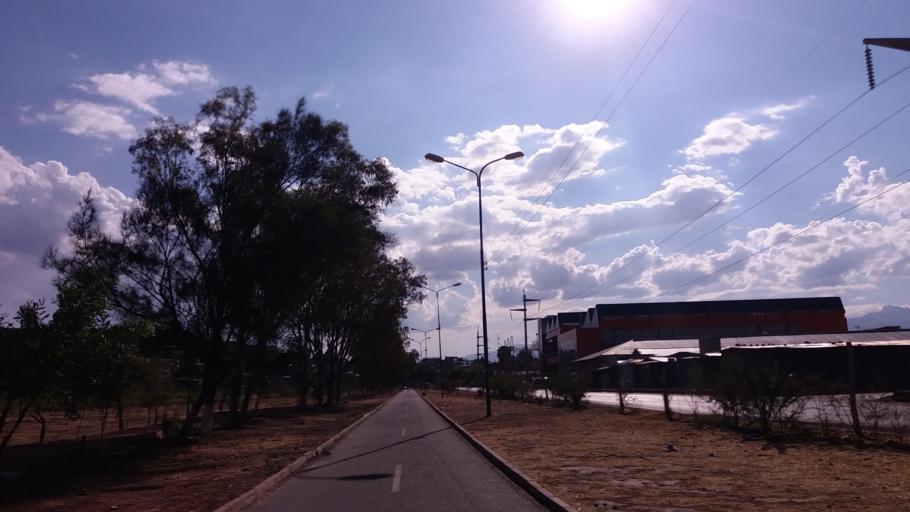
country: BO
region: Cochabamba
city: Cochabamba
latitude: -17.4006
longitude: -66.1418
